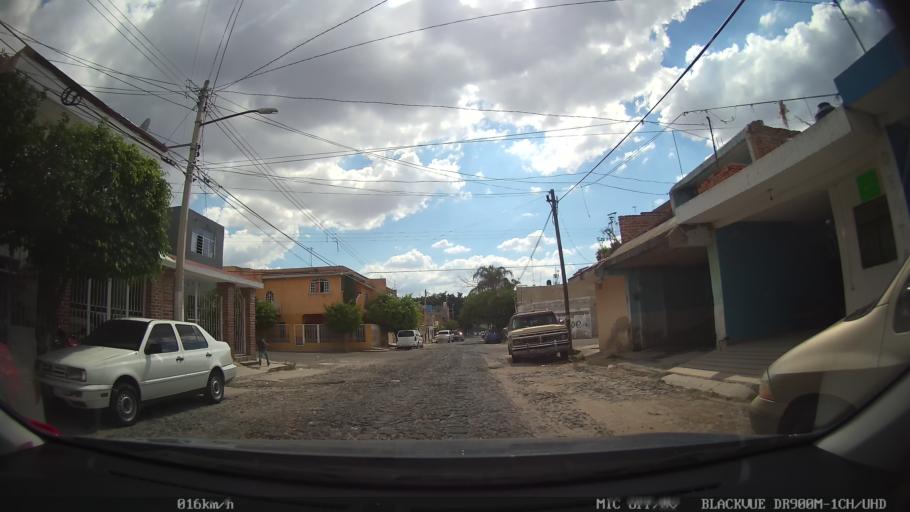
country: MX
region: Jalisco
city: Tlaquepaque
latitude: 20.6799
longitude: -103.2600
